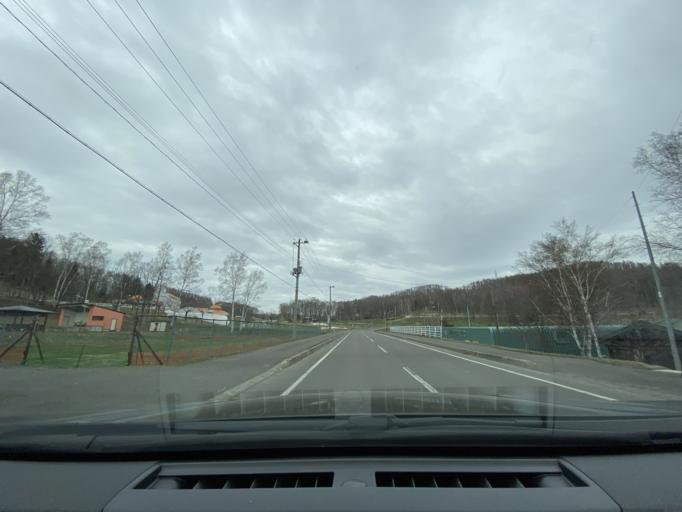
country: JP
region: Hokkaido
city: Nayoro
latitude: 44.0955
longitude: 142.4240
